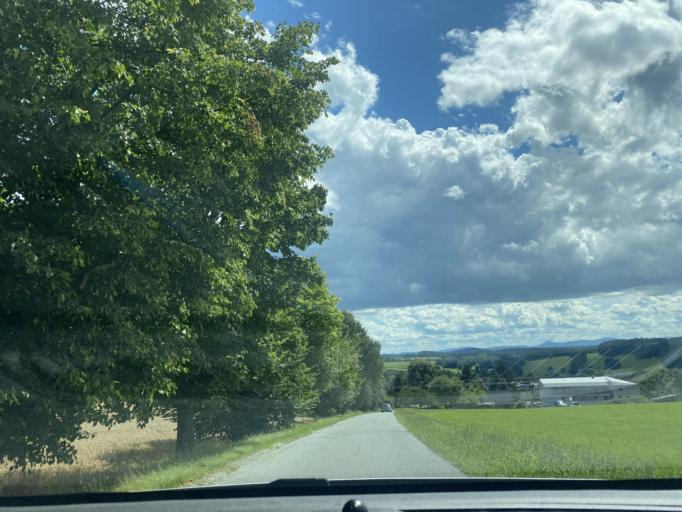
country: DE
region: Saxony
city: Beiersdorf
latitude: 51.0802
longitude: 14.5278
